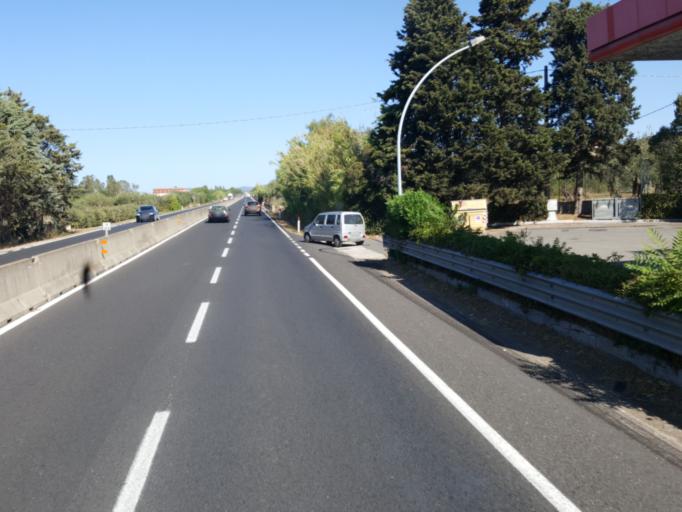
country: IT
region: Tuscany
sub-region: Provincia di Grosseto
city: Orbetello Scalo
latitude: 42.4590
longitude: 11.2473
